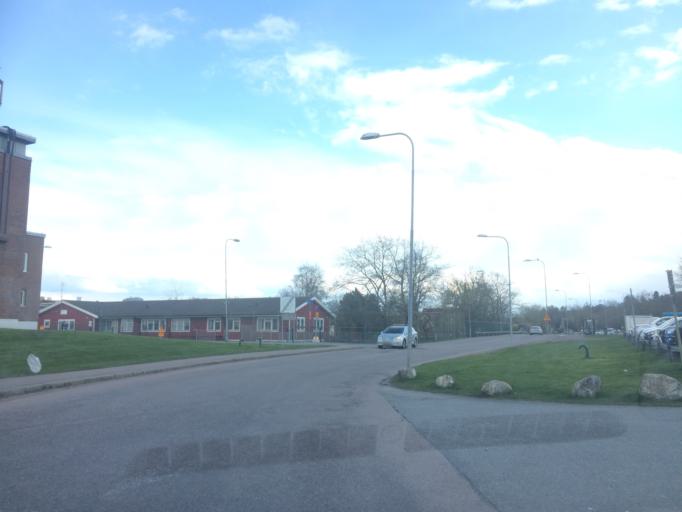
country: SE
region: Vaestra Goetaland
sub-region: Goteborg
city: Gardsten
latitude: 57.7932
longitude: 11.9911
